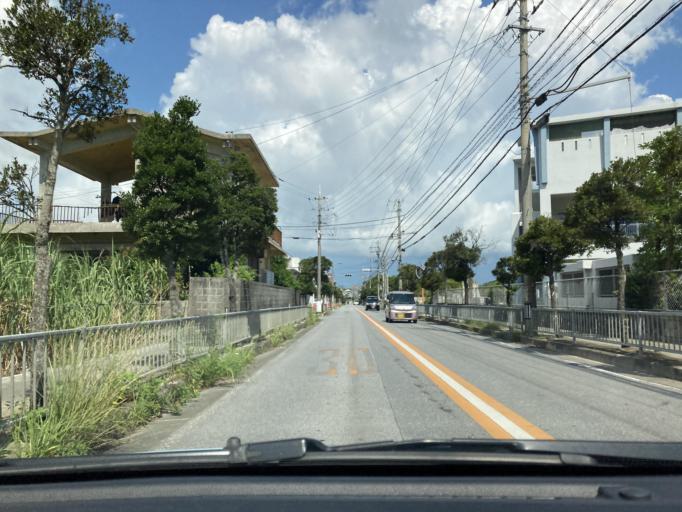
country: JP
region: Okinawa
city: Tomigusuku
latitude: 26.1526
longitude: 127.7514
